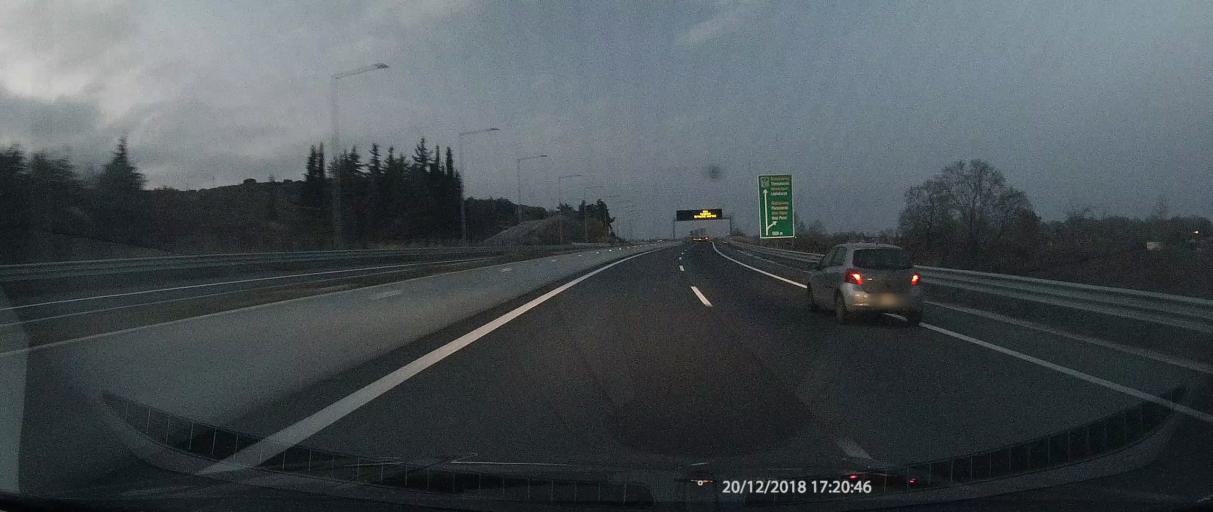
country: GR
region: Thessaly
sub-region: Nomos Larisis
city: Pyrgetos
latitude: 39.9705
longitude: 22.6398
